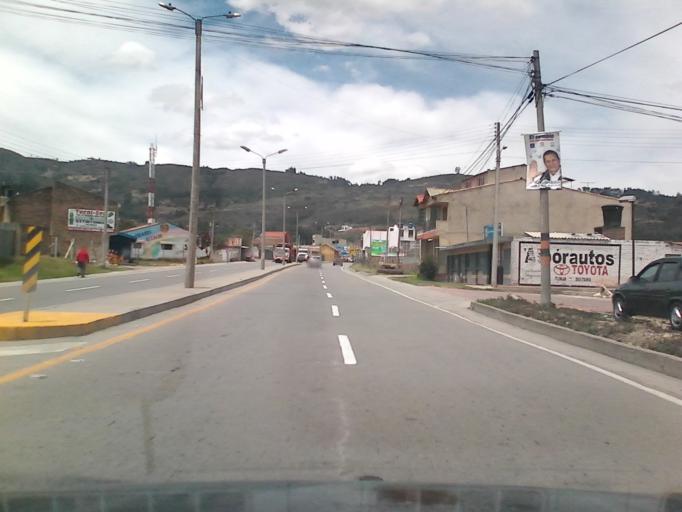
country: CO
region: Boyaca
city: Tibasosa
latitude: 5.7461
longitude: -72.9934
